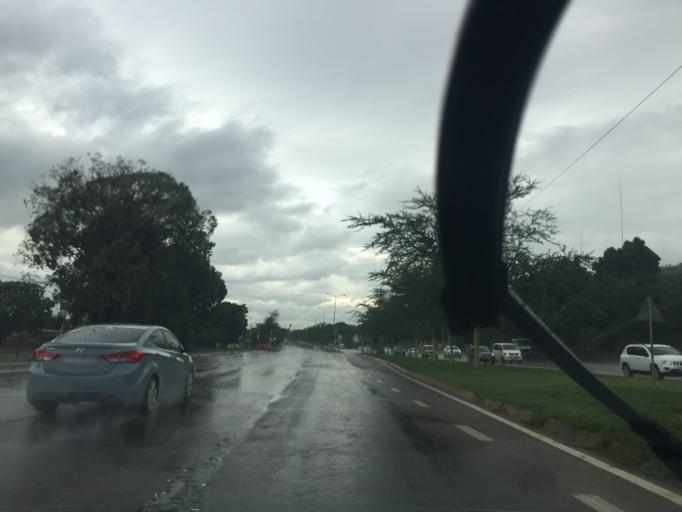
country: ZA
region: Gauteng
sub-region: City of Tshwane Metropolitan Municipality
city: Pretoria
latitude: -25.7671
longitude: 28.3007
